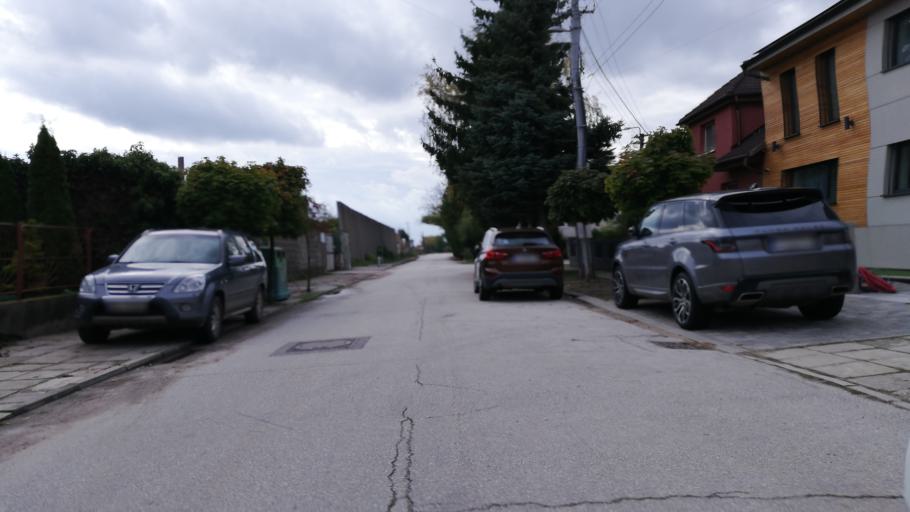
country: SK
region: Trnavsky
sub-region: Okres Skalica
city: Skalica
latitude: 48.8440
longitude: 17.2185
